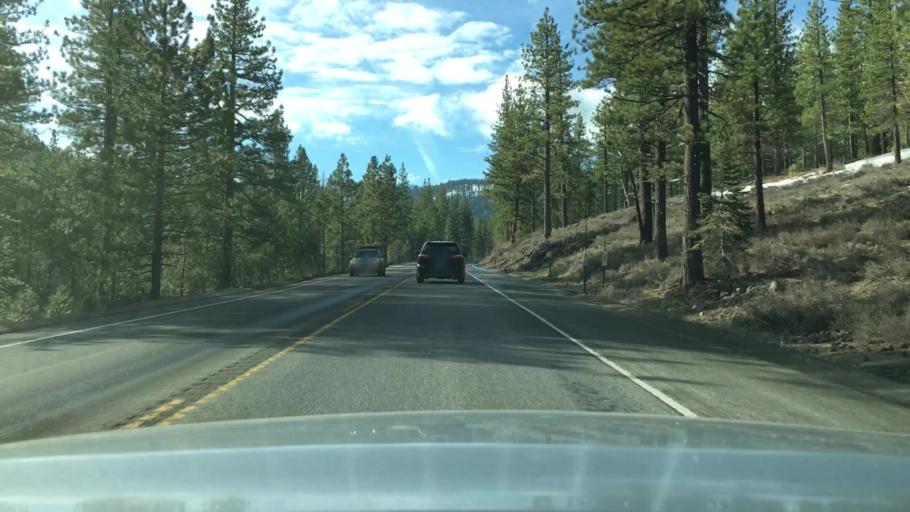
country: US
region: California
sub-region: Placer County
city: Tahoe Vista
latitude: 39.2937
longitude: -120.1040
